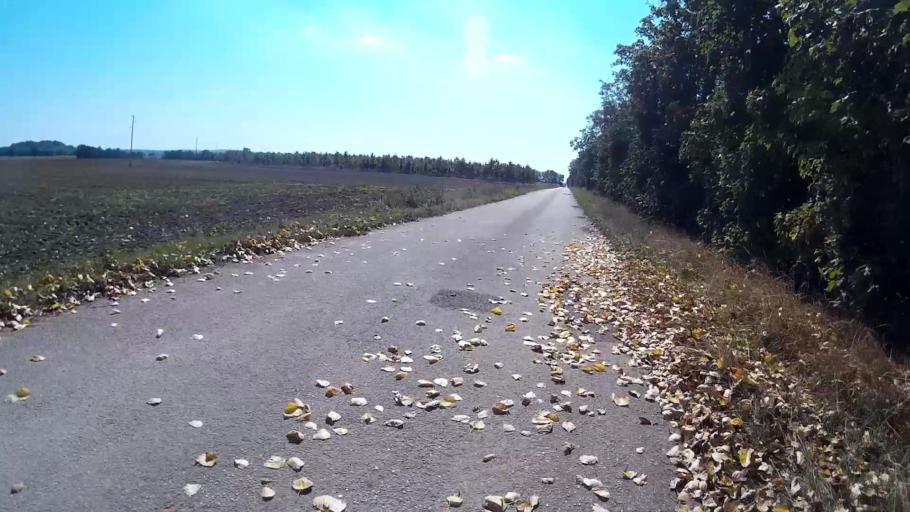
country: AT
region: Lower Austria
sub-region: Politischer Bezirk Mistelbach
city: Neudorf bei Staatz
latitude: 48.7780
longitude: 16.4877
